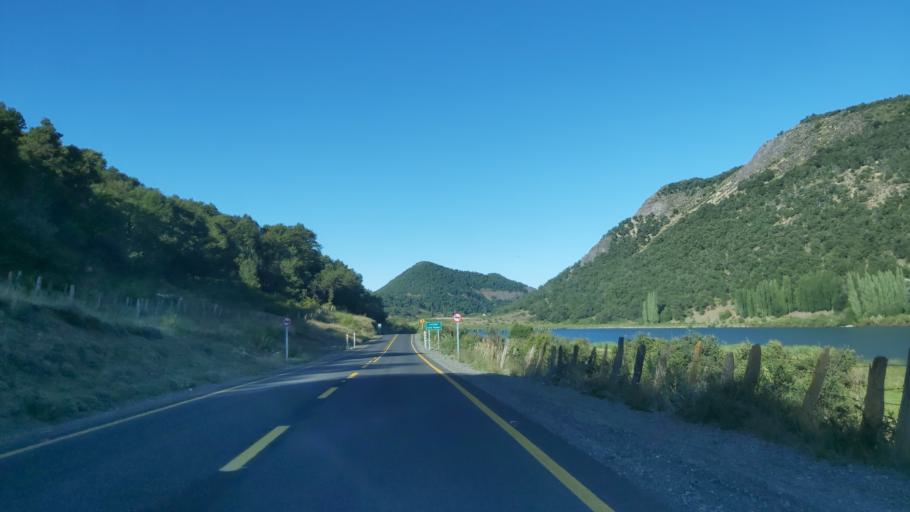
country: AR
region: Neuquen
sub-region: Departamento de Loncopue
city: Loncopue
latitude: -38.4415
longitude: -71.3376
